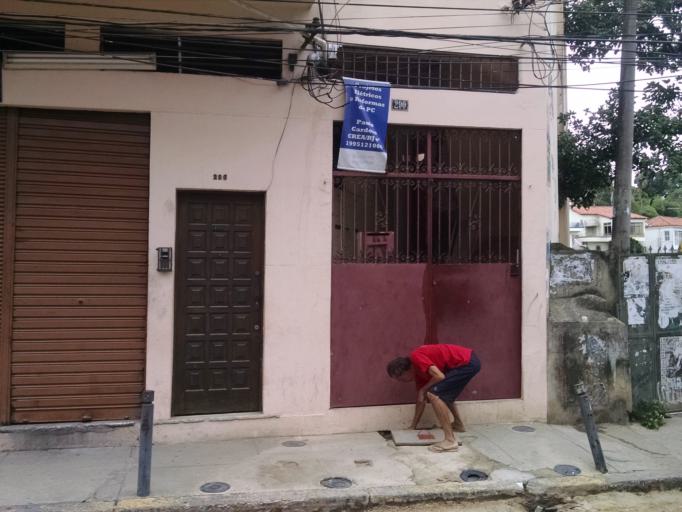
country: BR
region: Rio de Janeiro
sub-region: Rio De Janeiro
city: Rio de Janeiro
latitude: -22.9209
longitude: -43.1848
